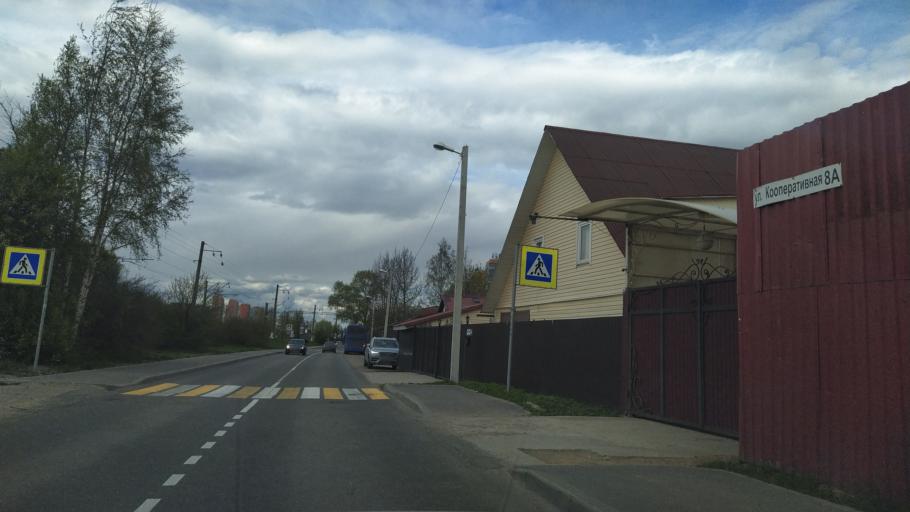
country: RU
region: Leningrad
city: Murino
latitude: 60.0453
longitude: 30.4404
